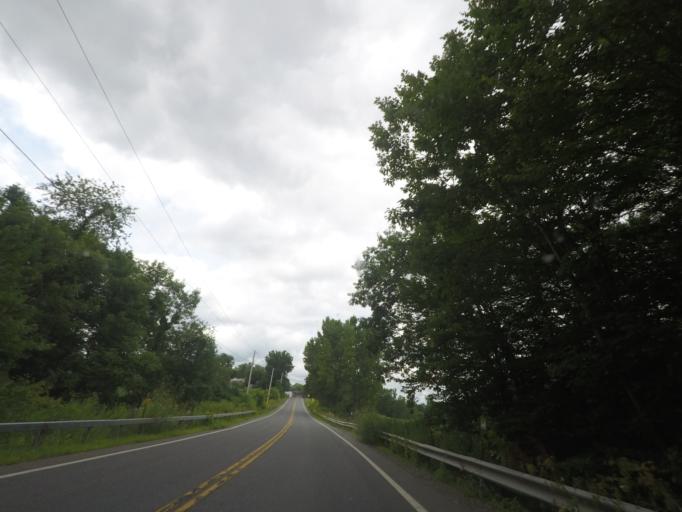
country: US
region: New York
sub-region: Saratoga County
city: Stillwater
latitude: 43.0070
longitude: -73.6943
